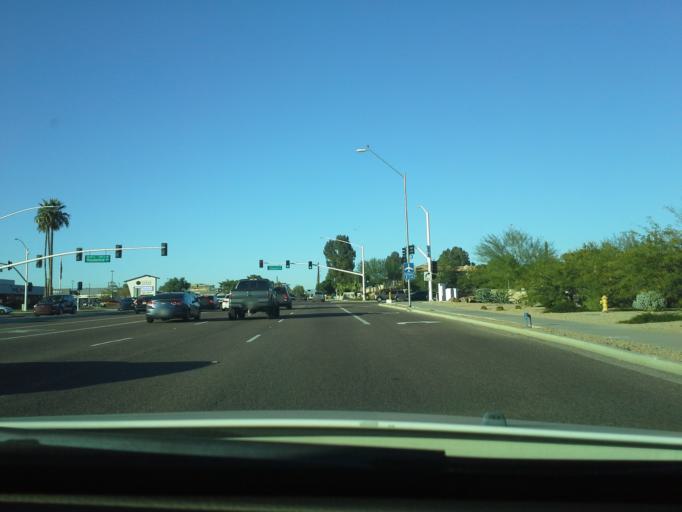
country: US
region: Arizona
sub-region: Maricopa County
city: Paradise Valley
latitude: 33.6104
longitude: -111.9257
